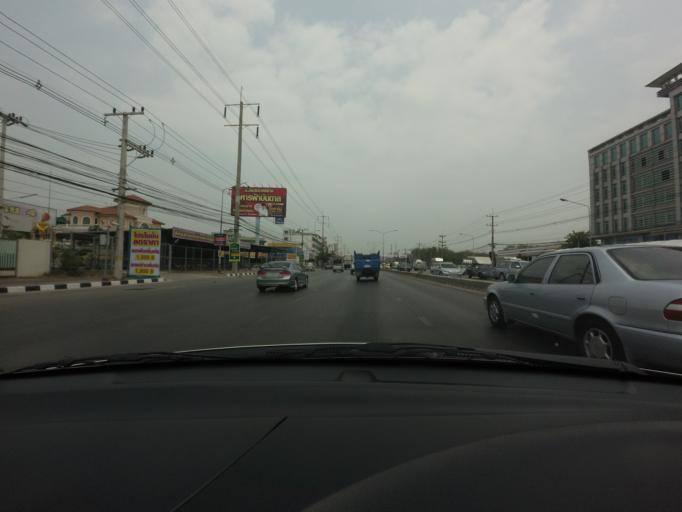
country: TH
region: Bangkok
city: Thawi Watthana
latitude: 13.7537
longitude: 100.3289
